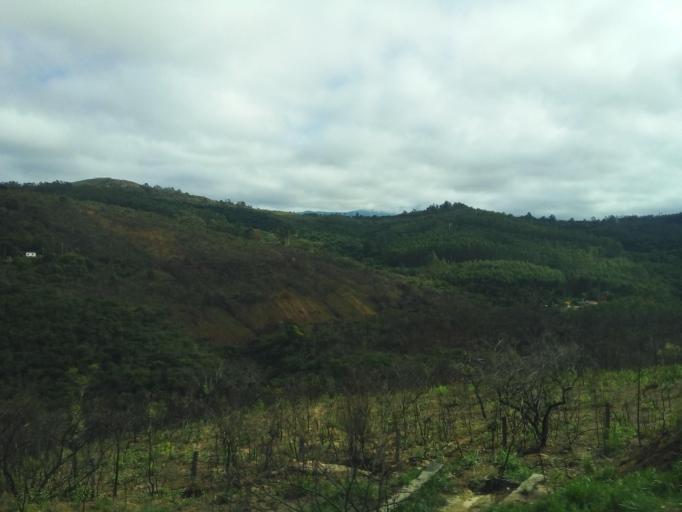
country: BR
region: Minas Gerais
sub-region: Caete
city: Caete
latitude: -19.9081
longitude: -43.6956
